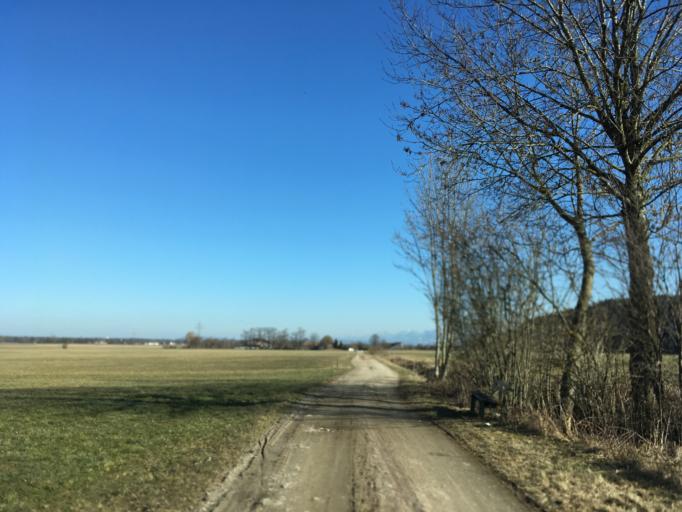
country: DE
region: Bavaria
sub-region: Upper Bavaria
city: Irschenberg
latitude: 47.8555
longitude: 11.9422
